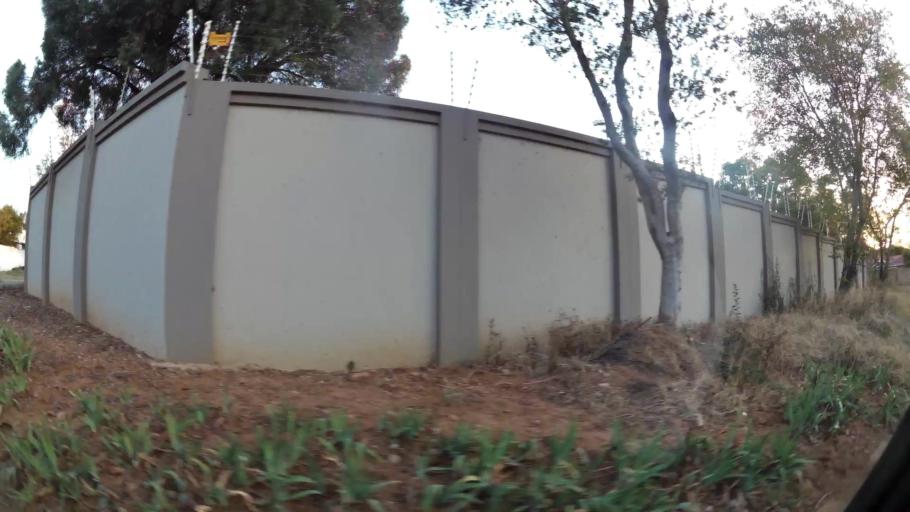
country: ZA
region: Gauteng
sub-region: City of Johannesburg Metropolitan Municipality
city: Diepsloot
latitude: -26.0282
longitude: 27.9894
